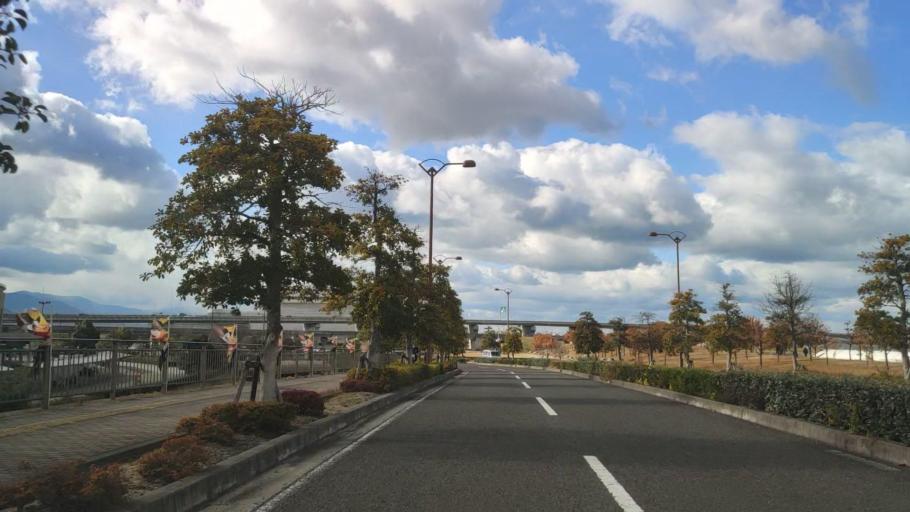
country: JP
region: Ehime
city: Masaki-cho
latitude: 33.8096
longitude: 132.7417
